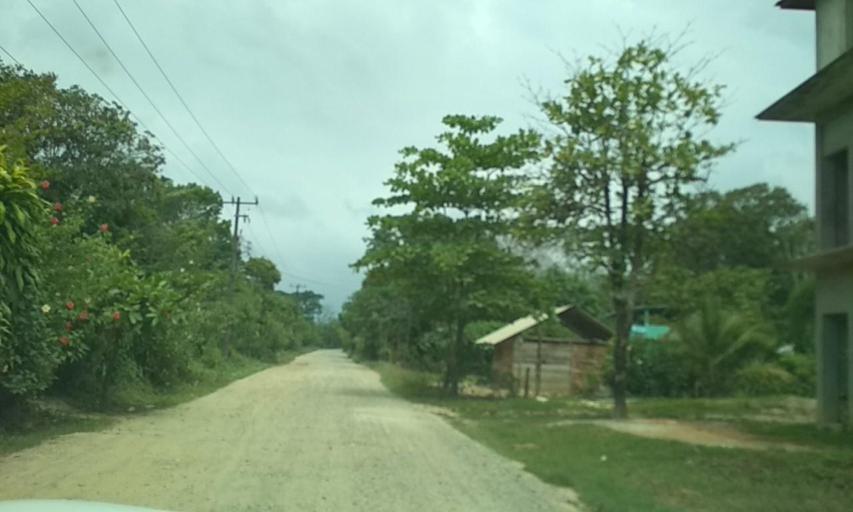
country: MX
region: Veracruz
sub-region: Uxpanapa
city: Poblado 10
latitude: 17.4982
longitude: -94.1453
